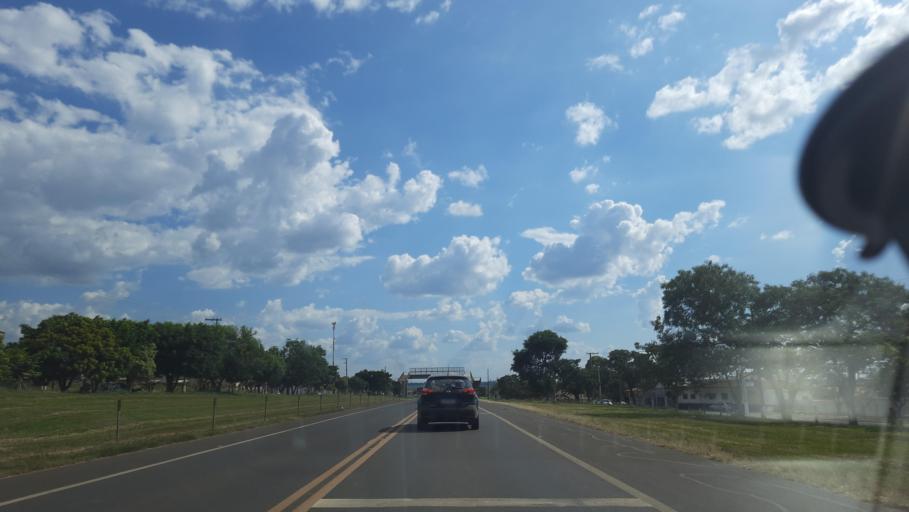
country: BR
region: Sao Paulo
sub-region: Casa Branca
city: Casa Branca
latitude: -21.7329
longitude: -46.9691
